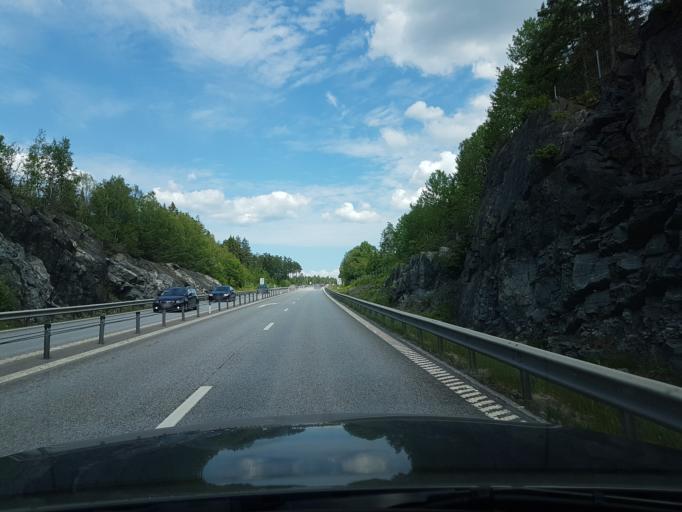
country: SE
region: Stockholm
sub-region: Osterakers Kommun
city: Akersberga
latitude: 59.5768
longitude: 18.2410
